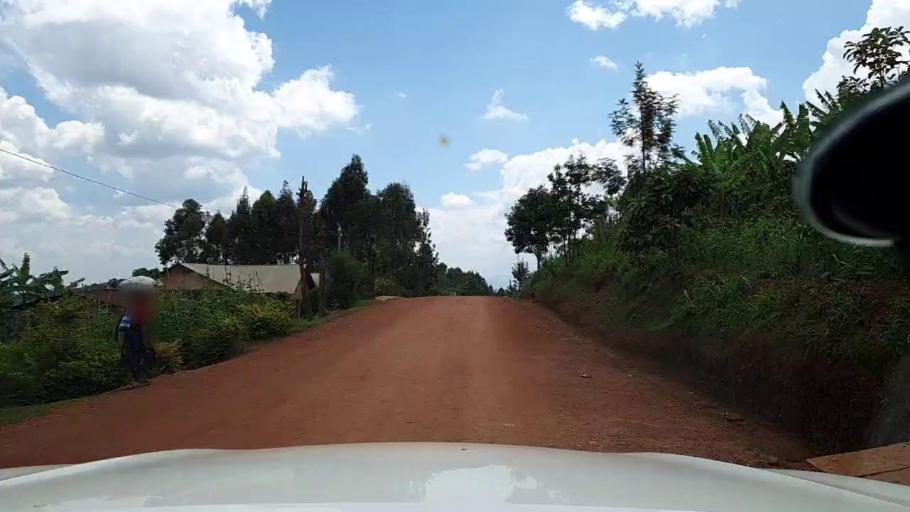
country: RW
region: Kigali
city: Kigali
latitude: -1.7963
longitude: 29.8448
